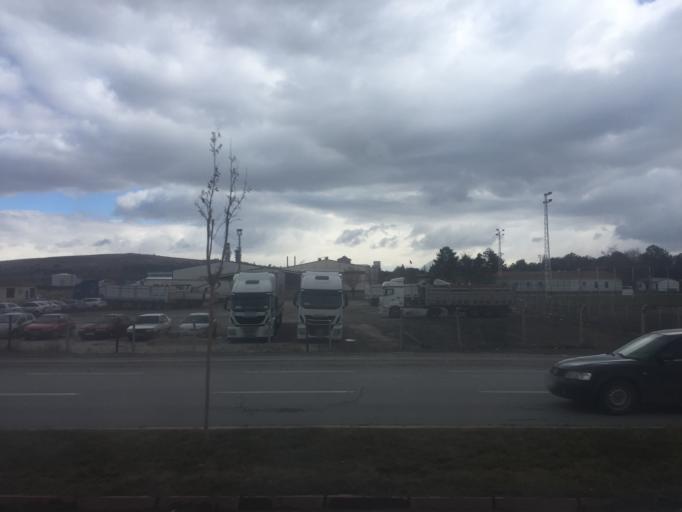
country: TR
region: Kayseri
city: Melikgazi
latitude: 38.7520
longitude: 35.4064
